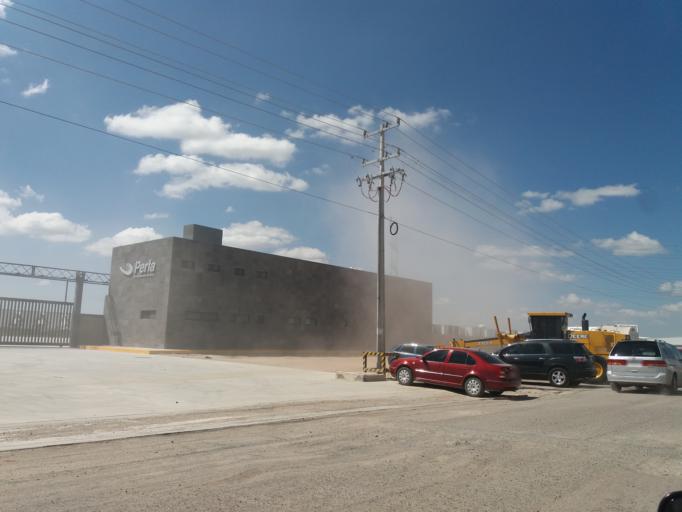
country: MX
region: Aguascalientes
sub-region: Aguascalientes
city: San Sebastian [Fraccionamiento]
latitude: 21.7982
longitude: -102.2867
